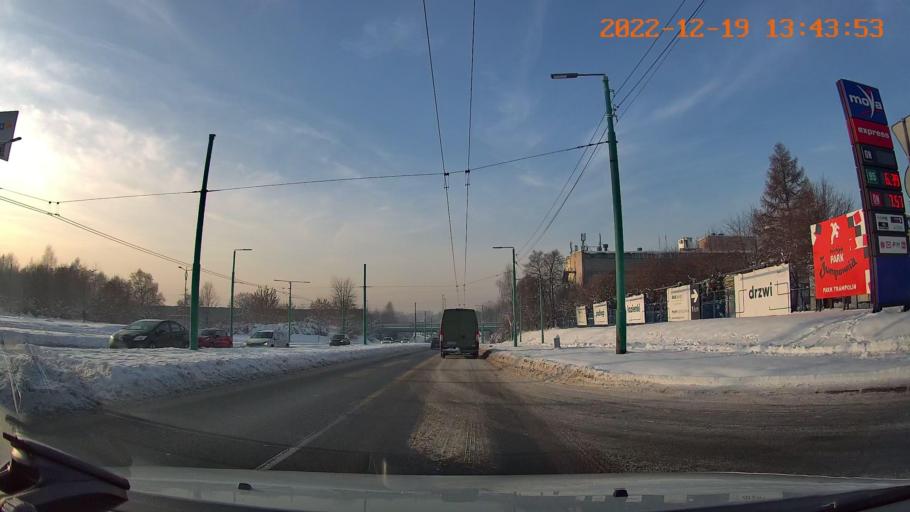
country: PL
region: Silesian Voivodeship
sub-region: Tychy
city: Cielmice
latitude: 50.1004
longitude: 19.0080
